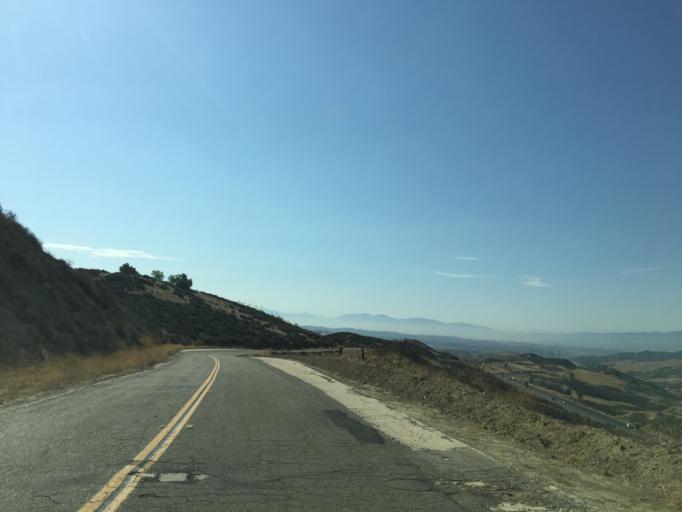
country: US
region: California
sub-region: Los Angeles County
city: Castaic
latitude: 34.5457
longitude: -118.6536
